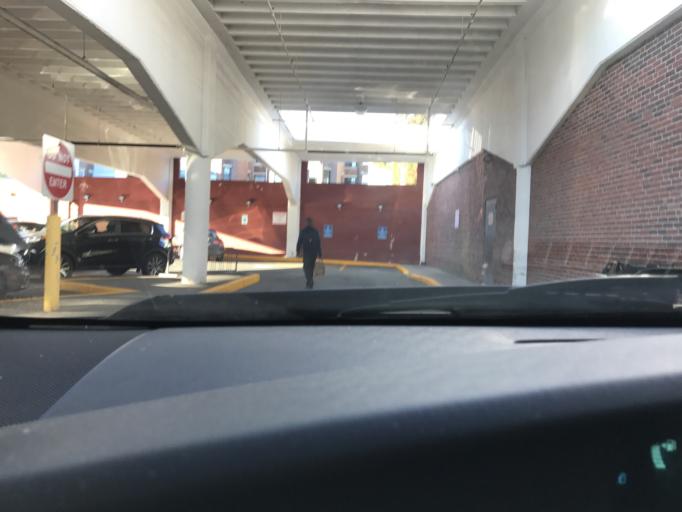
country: US
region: Massachusetts
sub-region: Norfolk County
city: Brookline
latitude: 42.3382
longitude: -71.1207
